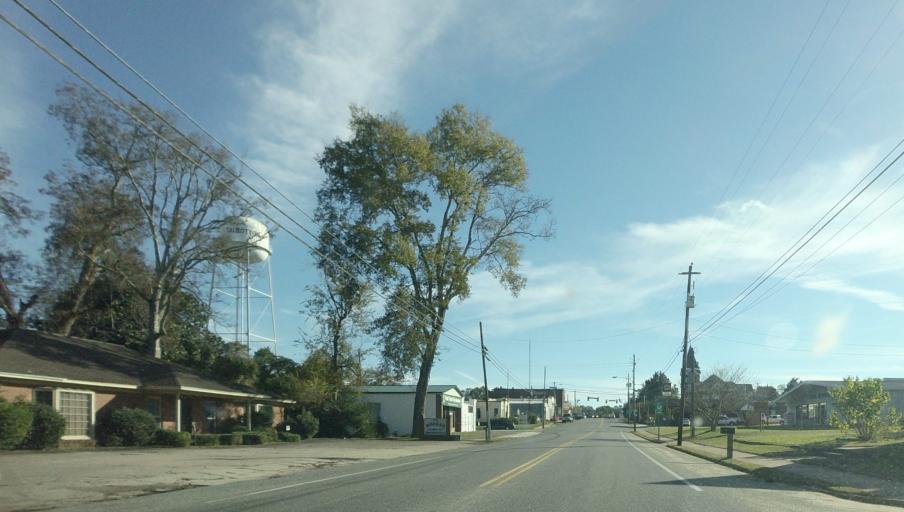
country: US
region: Georgia
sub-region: Talbot County
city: Talbotton
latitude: 32.6791
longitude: -84.5401
